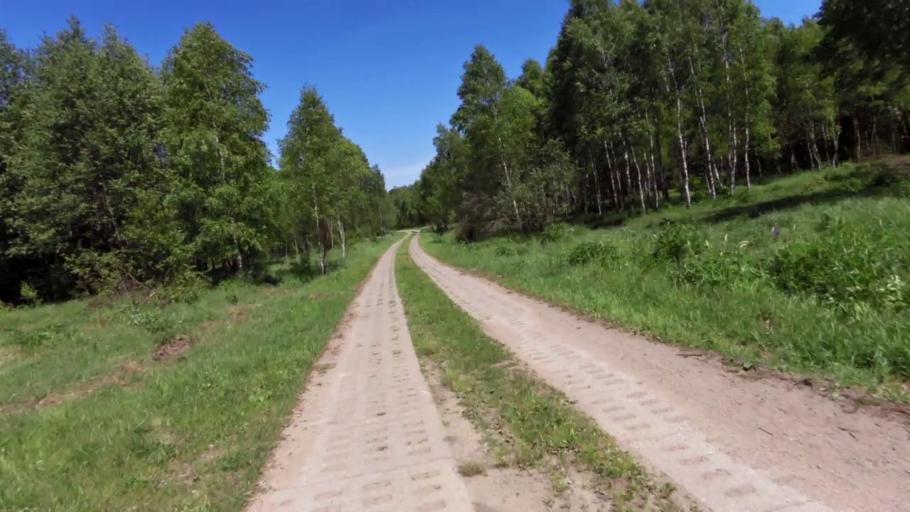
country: PL
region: West Pomeranian Voivodeship
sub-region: Powiat szczecinecki
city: Borne Sulinowo
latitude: 53.5769
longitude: 16.6402
